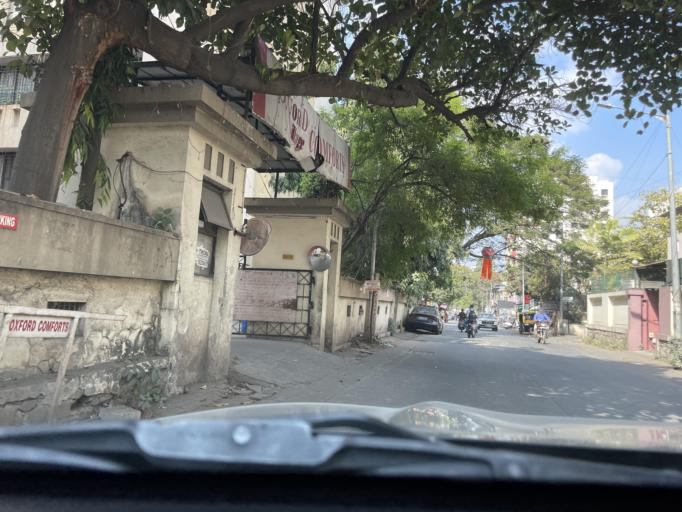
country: IN
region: Maharashtra
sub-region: Pune Division
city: Pune
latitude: 18.4824
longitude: 73.9006
